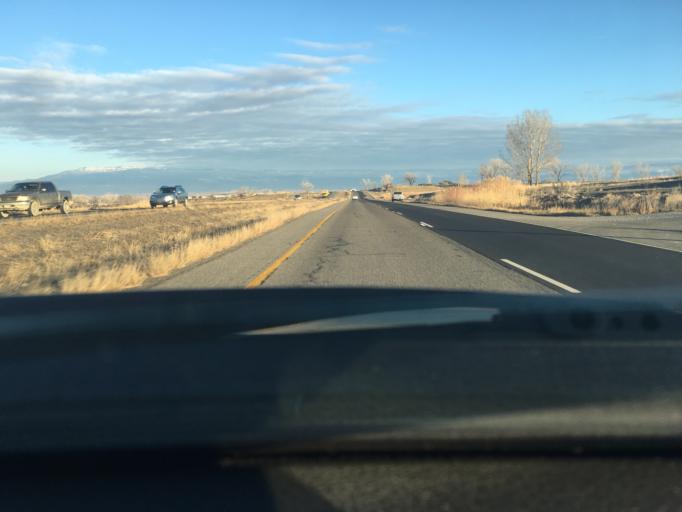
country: US
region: Colorado
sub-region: Montrose County
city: Olathe
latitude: 38.6267
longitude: -107.9852
